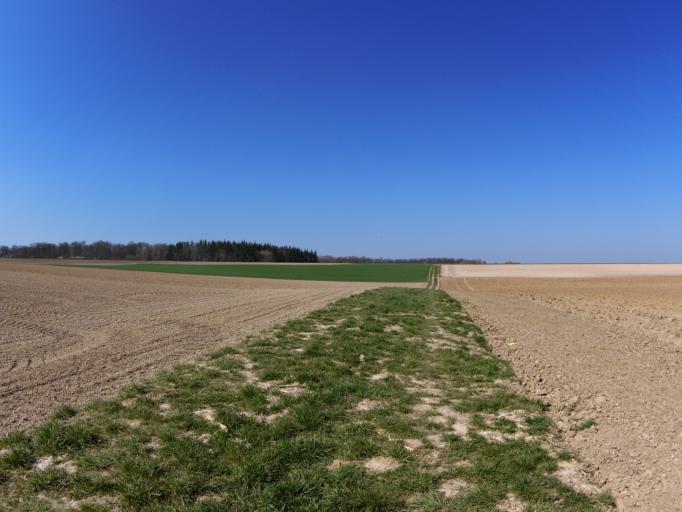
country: DE
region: Bavaria
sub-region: Regierungsbezirk Unterfranken
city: Oberpleichfeld
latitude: 49.8379
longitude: 10.0742
